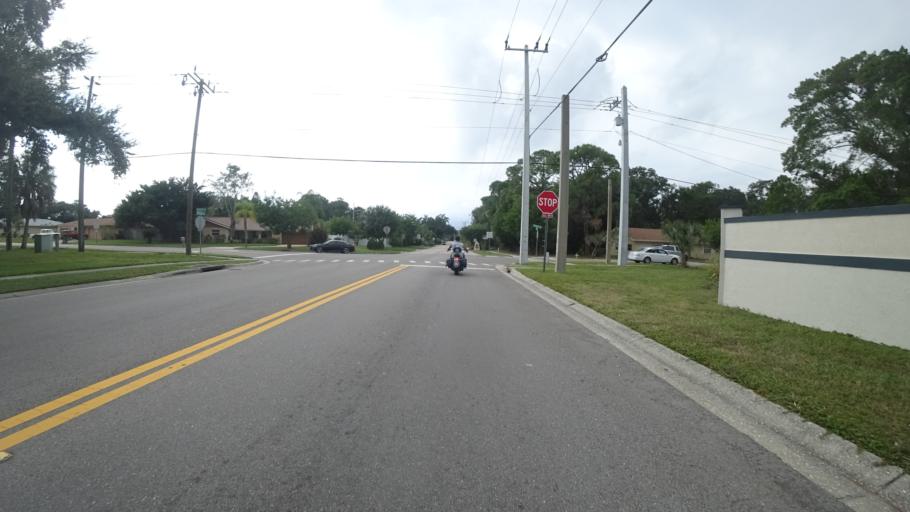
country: US
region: Florida
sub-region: Manatee County
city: Whitfield
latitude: 27.4184
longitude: -82.5546
